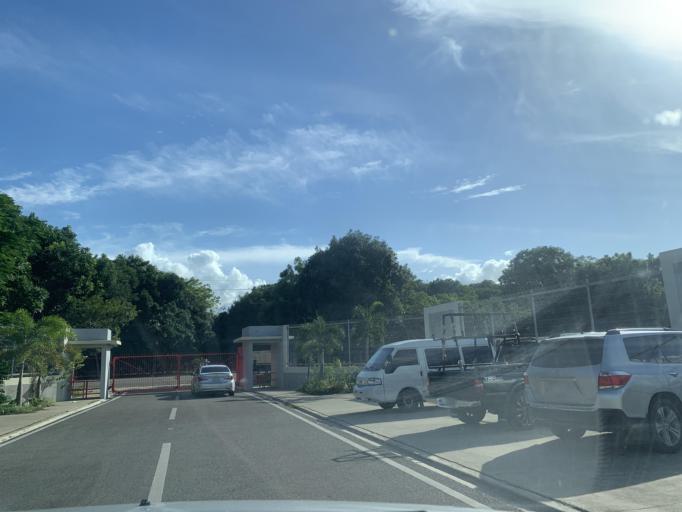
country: DO
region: Santiago
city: Santiago de los Caballeros
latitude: 19.4686
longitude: -70.6959
